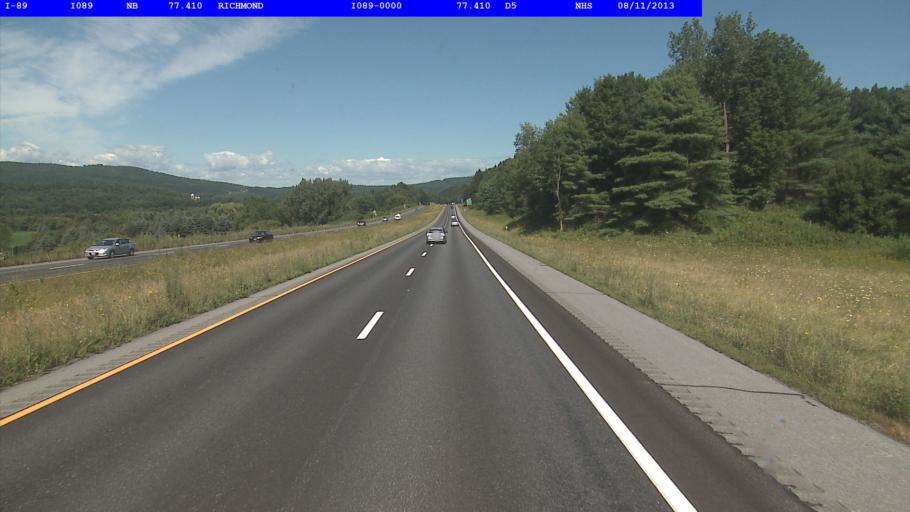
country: US
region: Vermont
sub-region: Chittenden County
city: Williston
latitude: 44.4157
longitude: -72.9947
